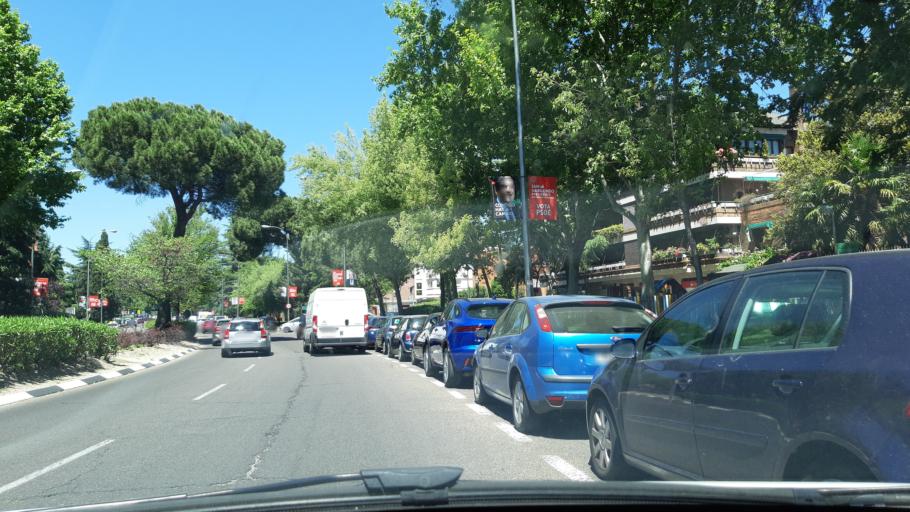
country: ES
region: Madrid
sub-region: Provincia de Madrid
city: Ciudad Lineal
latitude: 40.4426
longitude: -3.6414
